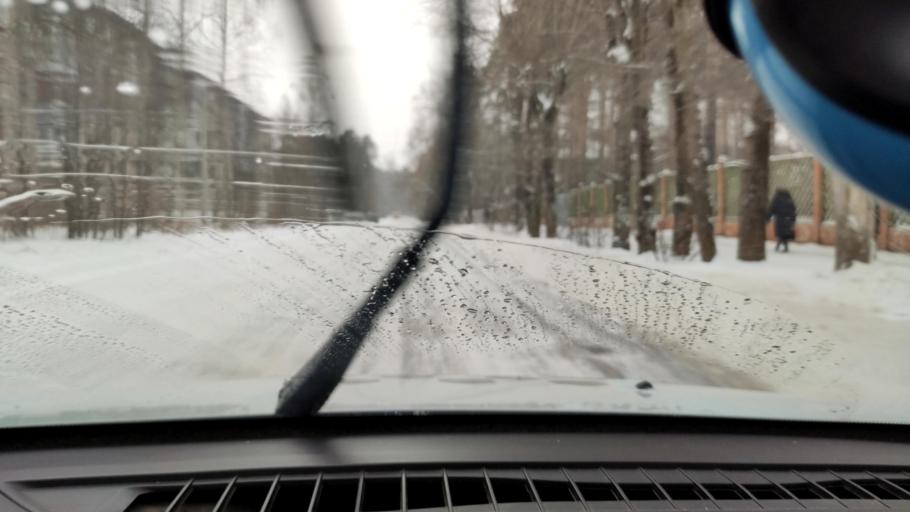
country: RU
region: Perm
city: Kondratovo
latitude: 58.0255
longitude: 56.0118
